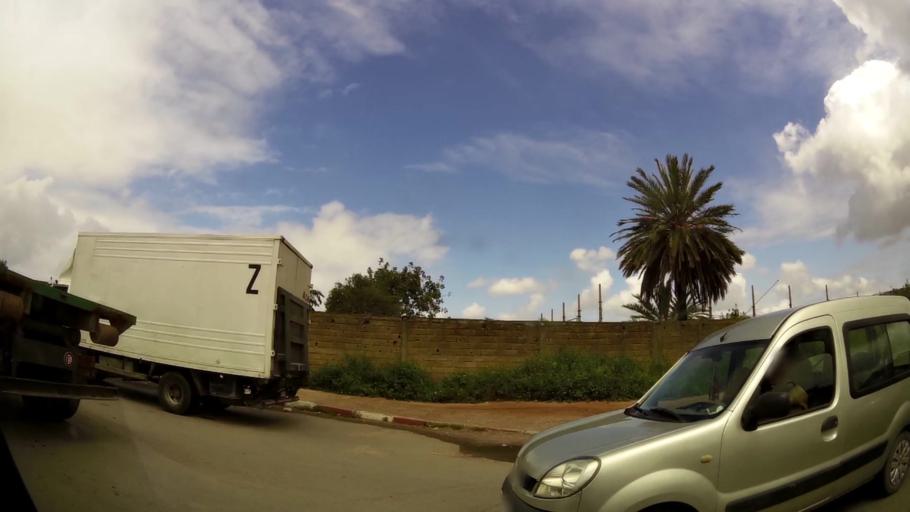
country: MA
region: Grand Casablanca
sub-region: Mediouna
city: Tit Mellil
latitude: 33.6065
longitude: -7.4945
